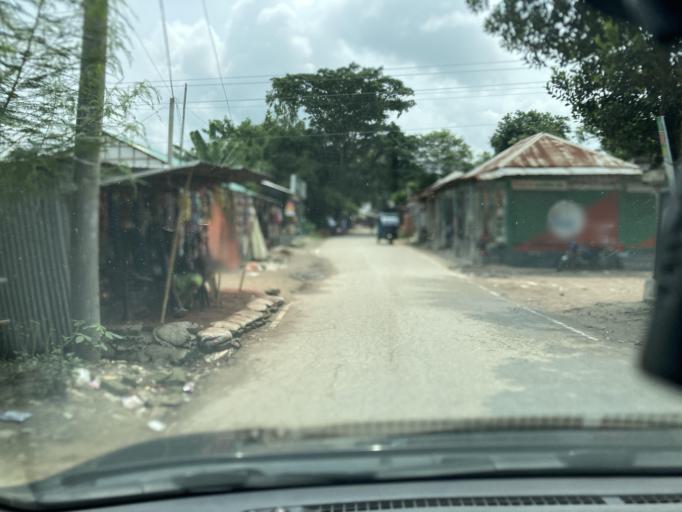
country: BD
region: Dhaka
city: Dohar
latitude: 23.7612
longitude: 90.2011
